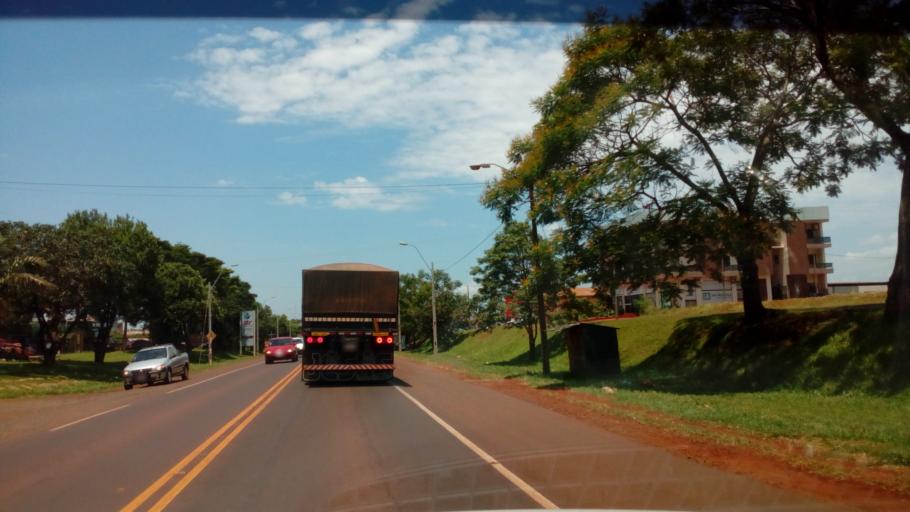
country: PY
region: Alto Parana
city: Santa Rita
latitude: -25.8089
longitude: -55.1009
